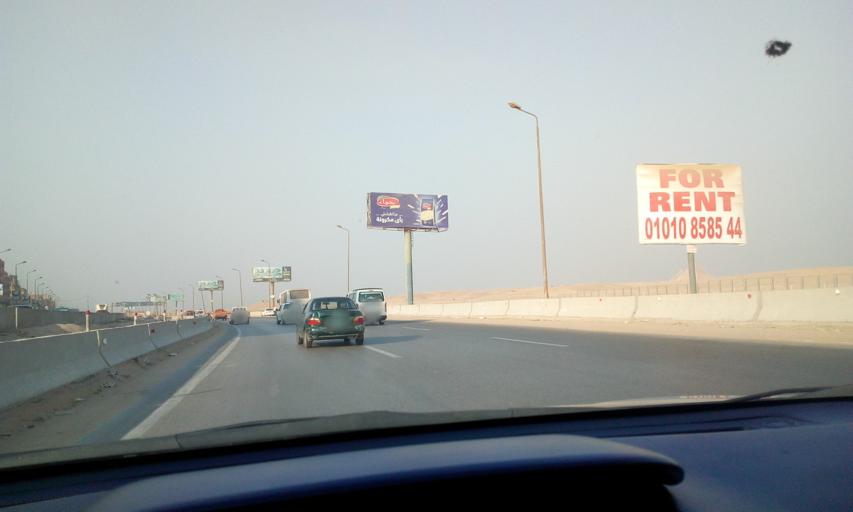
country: EG
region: Al Jizah
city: Al Jizah
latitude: 29.9592
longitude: 31.1082
